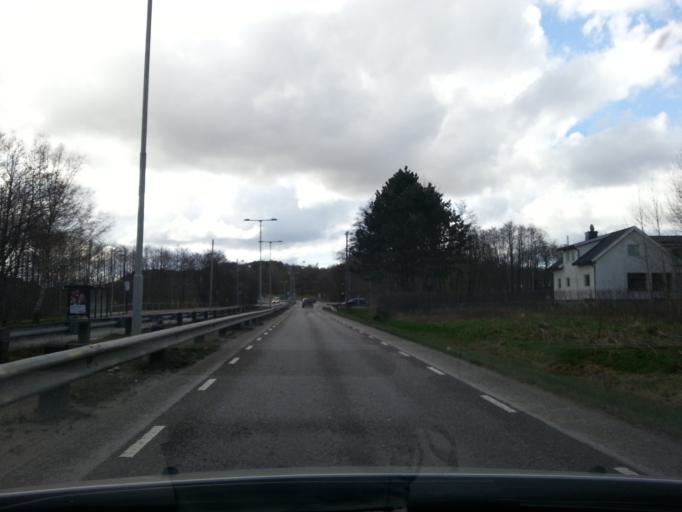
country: SE
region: Vaestra Goetaland
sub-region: Goteborg
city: Goeteborg
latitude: 57.7539
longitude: 11.9395
